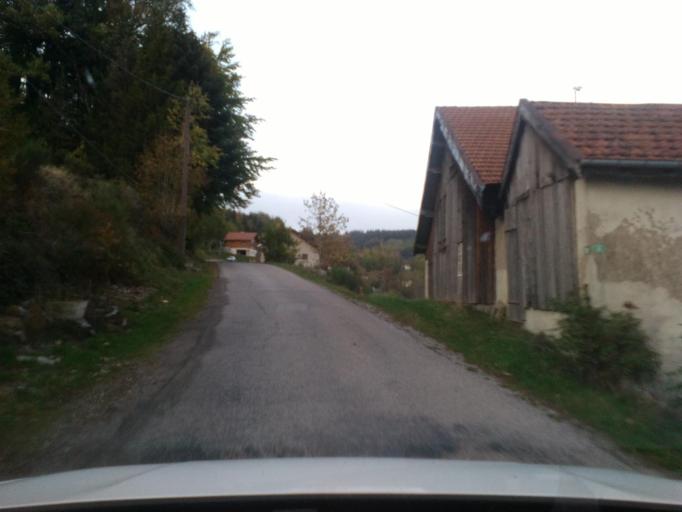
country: FR
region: Lorraine
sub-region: Departement des Vosges
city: Le Tholy
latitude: 48.0722
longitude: 6.7330
